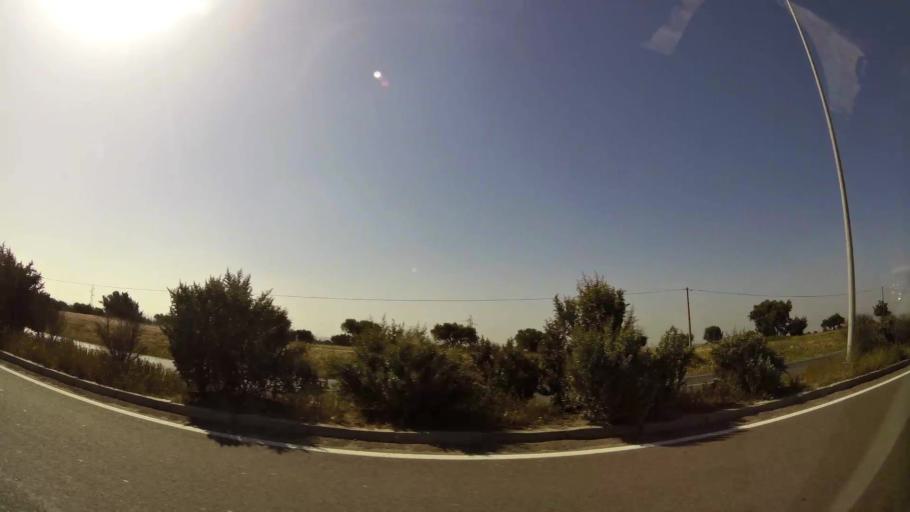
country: MA
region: Souss-Massa-Draa
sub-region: Inezgane-Ait Mellou
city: Inezgane
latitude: 30.3939
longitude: -9.4650
